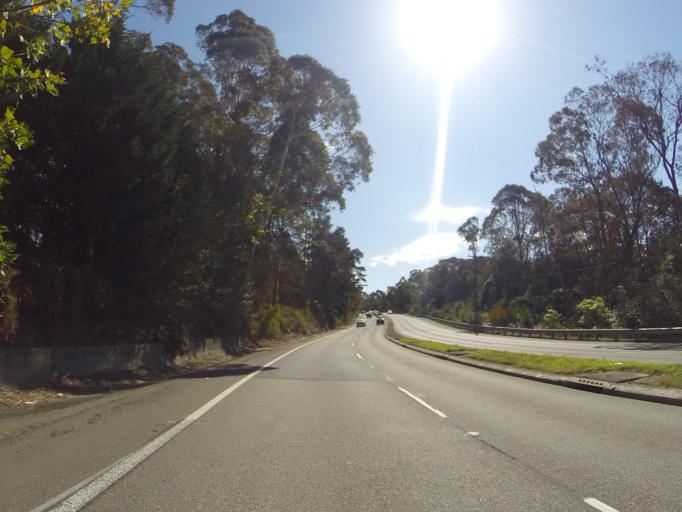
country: AU
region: New South Wales
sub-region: Blue Mountains Municipality
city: Blaxland
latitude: -33.7019
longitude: 150.5751
